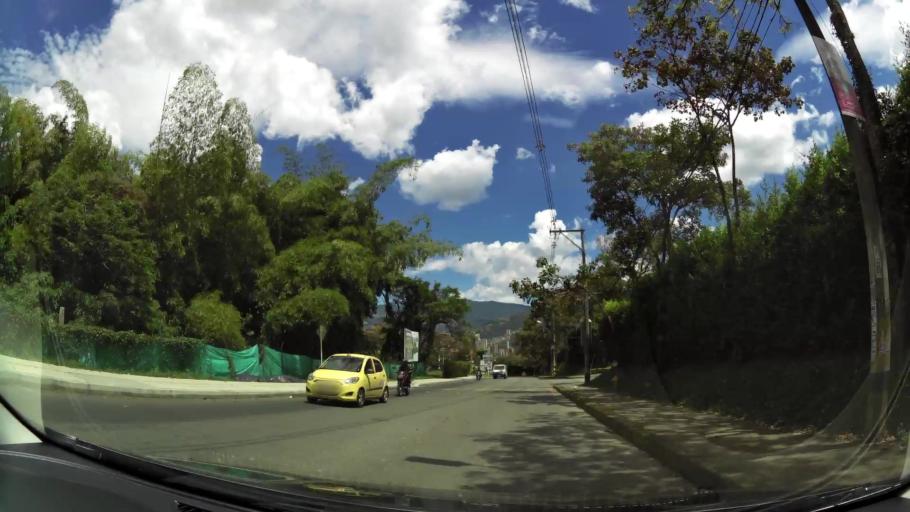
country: CO
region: Antioquia
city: La Estrella
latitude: 6.1609
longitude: -75.6294
